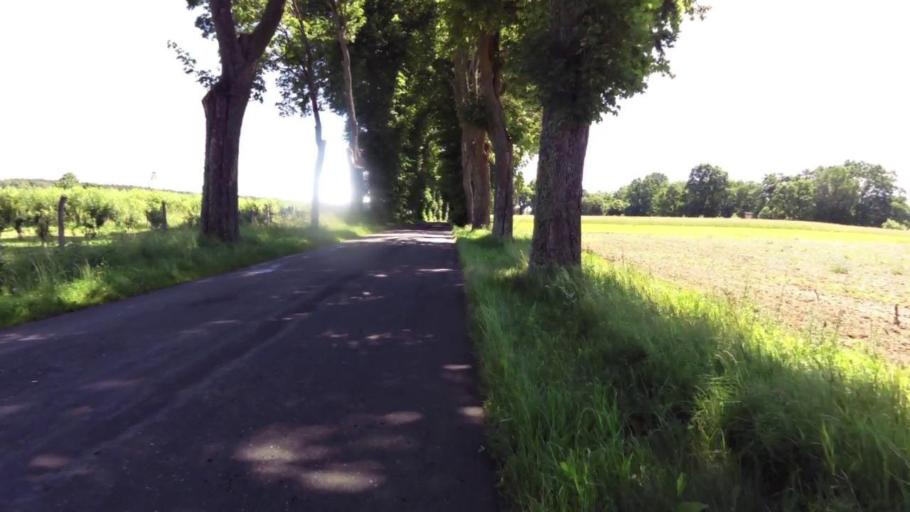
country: PL
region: West Pomeranian Voivodeship
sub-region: Powiat swidwinski
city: Polczyn-Zdroj
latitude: 53.9008
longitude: 16.0821
